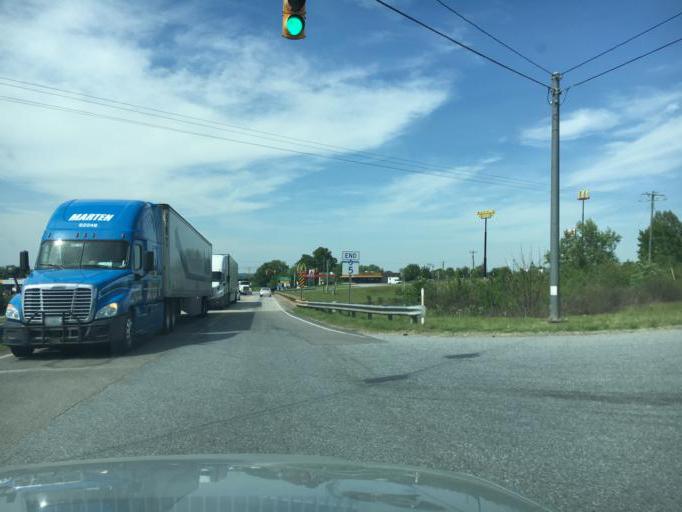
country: US
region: South Carolina
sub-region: Cherokee County
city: Blacksburg
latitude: 35.1402
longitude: -81.5087
